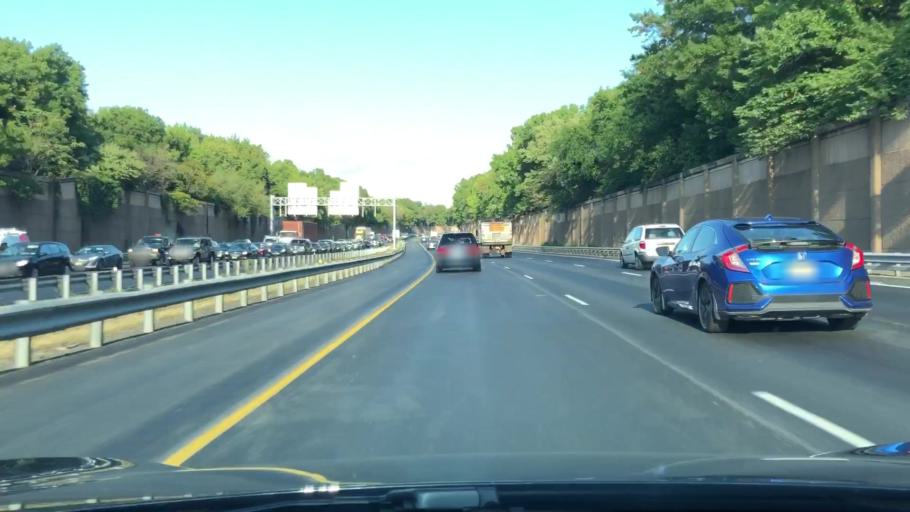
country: US
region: New Jersey
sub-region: Camden County
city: Haddon Heights
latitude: 39.8730
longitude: -75.0611
